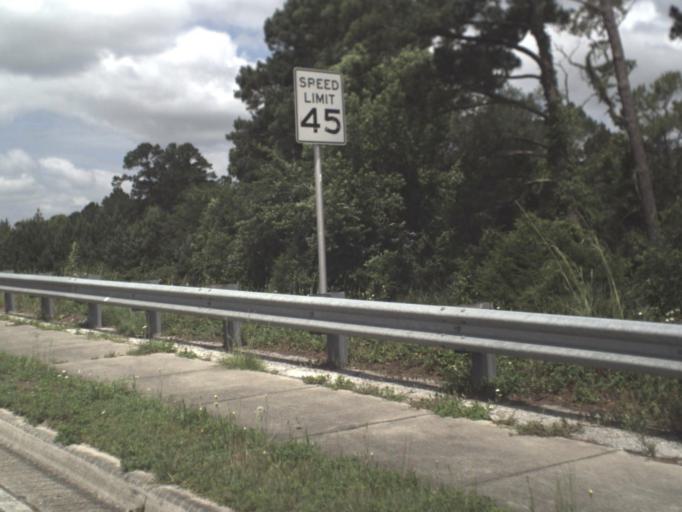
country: US
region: Florida
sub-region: Nassau County
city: Callahan
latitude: 30.5588
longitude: -81.8344
